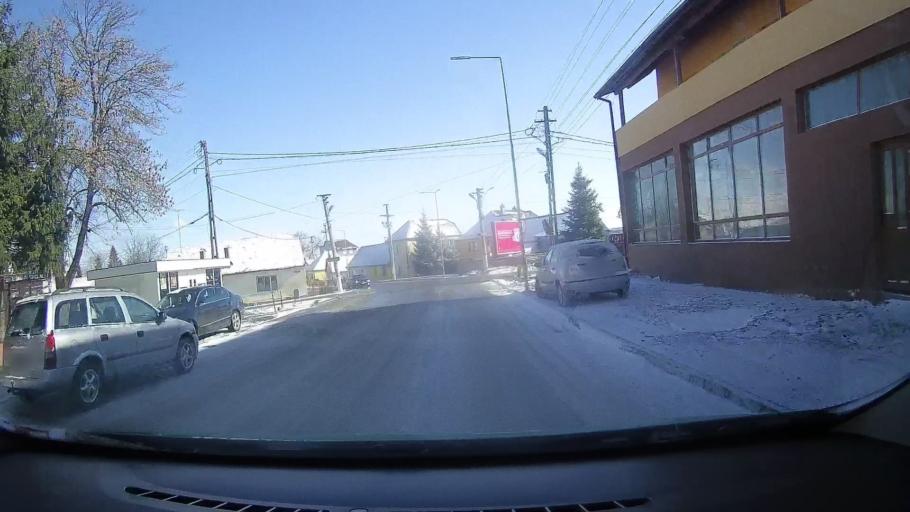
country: RO
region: Sibiu
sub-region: Comuna Avrig
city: Avrig
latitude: 45.7297
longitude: 24.3791
